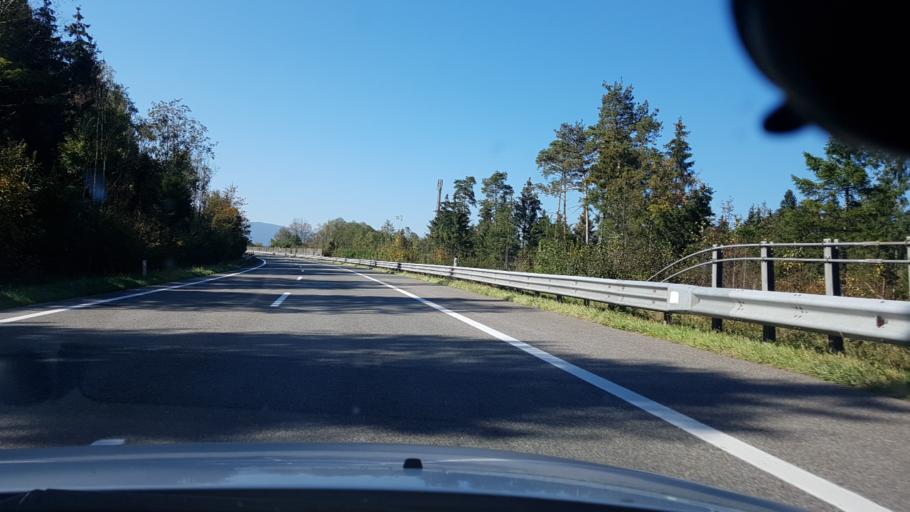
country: DE
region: Bavaria
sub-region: Upper Bavaria
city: Ainring
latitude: 47.7711
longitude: 12.9804
